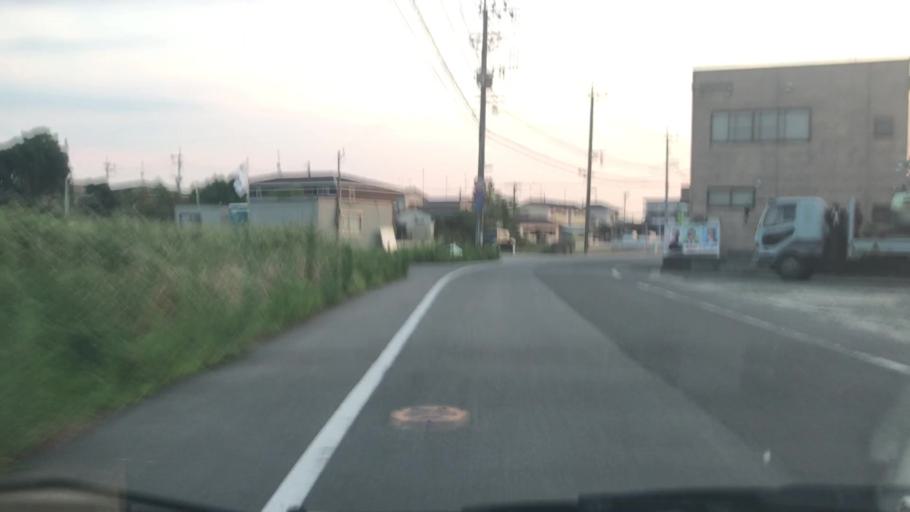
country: JP
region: Saga Prefecture
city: Saga-shi
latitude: 33.2550
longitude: 130.2867
